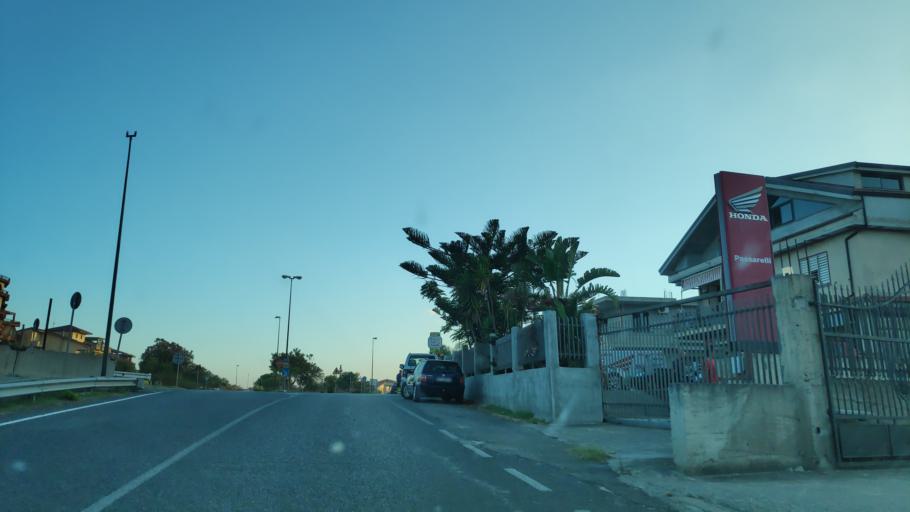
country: IT
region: Calabria
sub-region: Provincia di Reggio Calabria
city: Marina di Gioiosa Ionica
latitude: 38.2940
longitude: 16.3208
